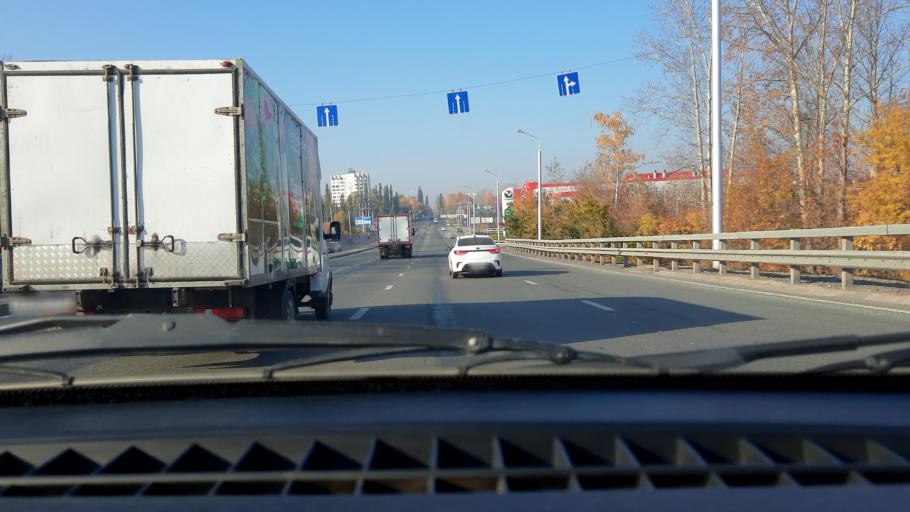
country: RU
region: Bashkortostan
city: Mikhaylovka
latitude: 54.7061
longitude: 55.8512
